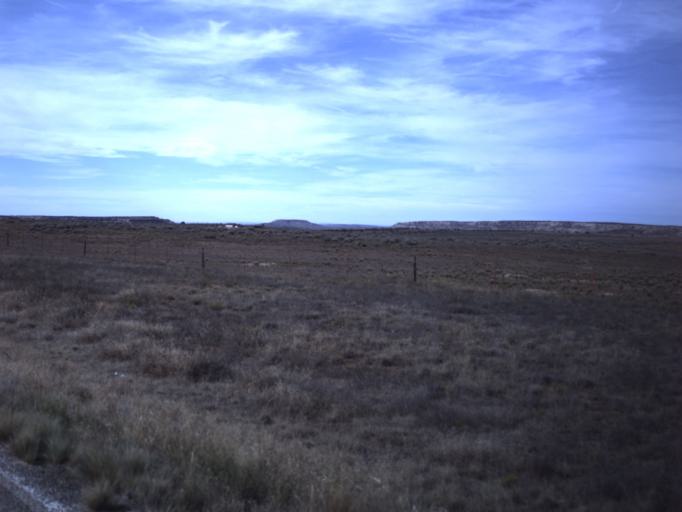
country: US
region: Utah
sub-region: San Juan County
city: Blanding
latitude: 37.3904
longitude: -109.3395
